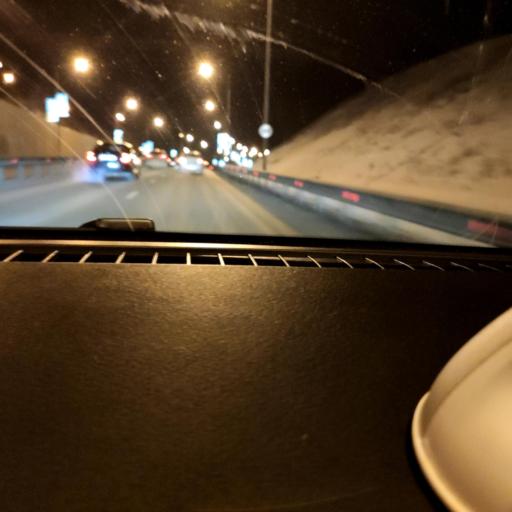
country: RU
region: Samara
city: Volzhskiy
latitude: 53.3708
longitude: 50.1852
